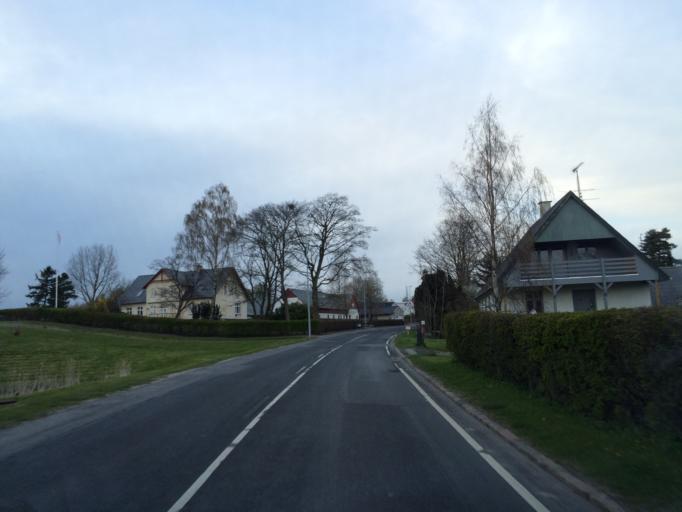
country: DK
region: South Denmark
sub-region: Odense Kommune
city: Bellinge
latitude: 55.3740
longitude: 10.2649
